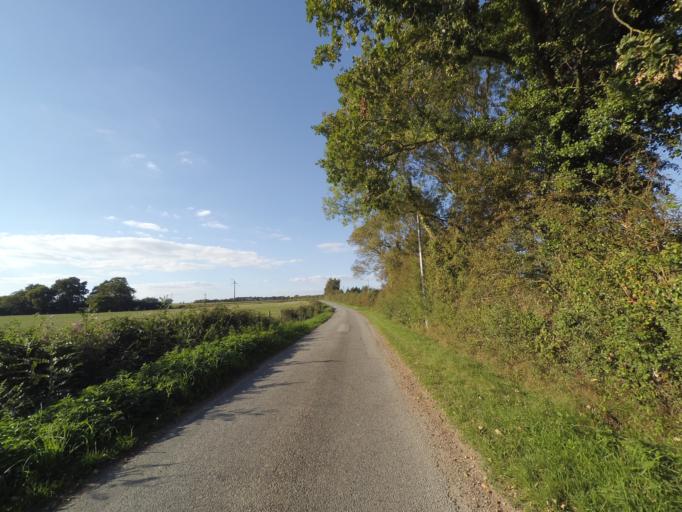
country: FR
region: Pays de la Loire
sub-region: Departement de la Loire-Atlantique
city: Chemere
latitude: 47.1364
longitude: -1.9117
